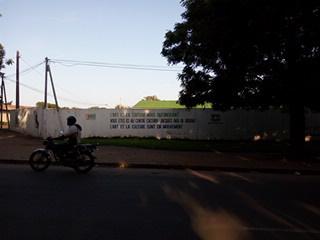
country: CI
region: Vallee du Bandama
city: Bouake
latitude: 7.6853
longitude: -5.0257
